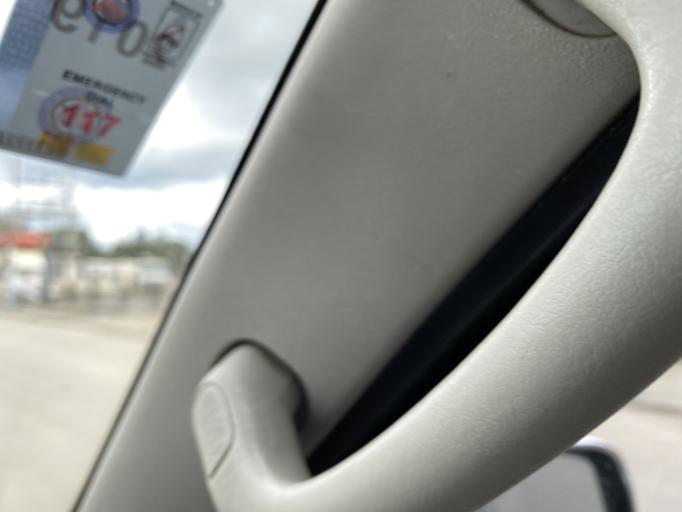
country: PH
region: Central Visayas
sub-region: Province of Bohol
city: Tagbilaran City
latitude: 9.6547
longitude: 123.8690
